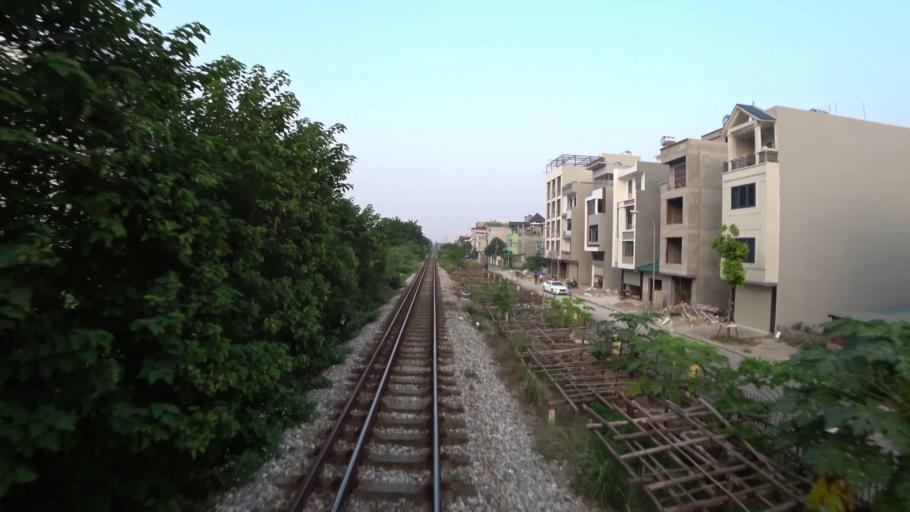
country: VN
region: Ha Noi
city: Trau Quy
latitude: 21.0841
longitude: 105.9147
